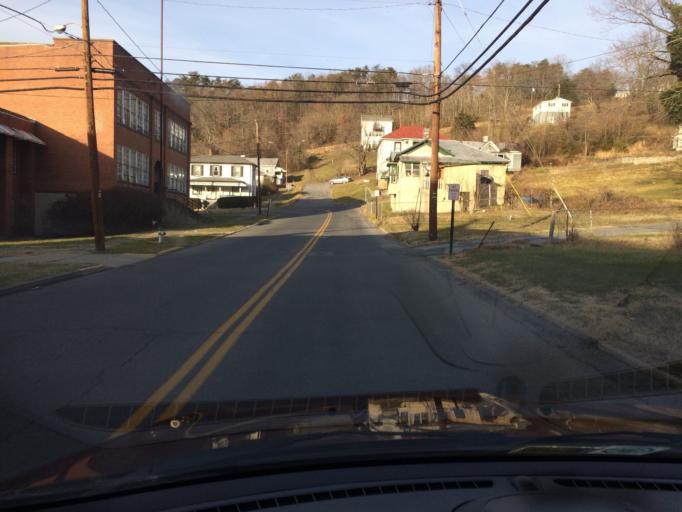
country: US
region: Virginia
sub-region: Alleghany County
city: Clifton Forge
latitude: 37.8154
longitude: -79.8189
